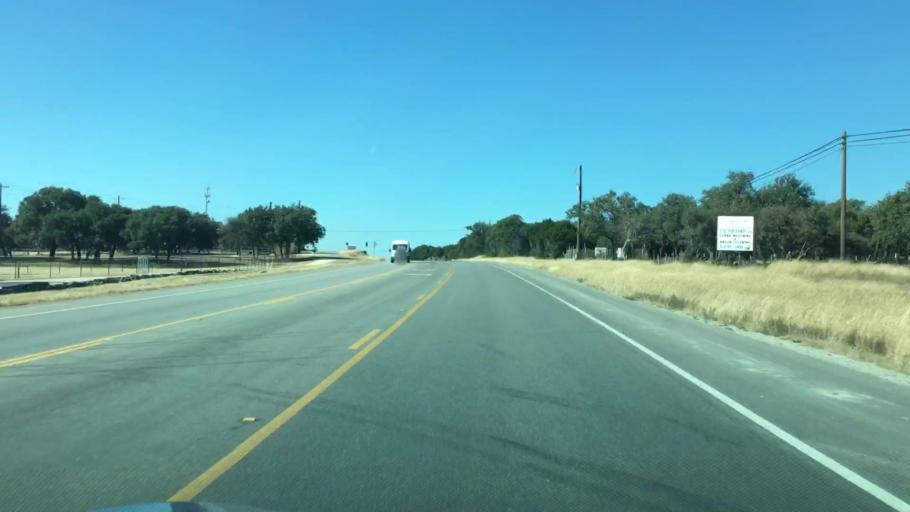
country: US
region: Texas
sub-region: Hays County
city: Dripping Springs
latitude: 30.2083
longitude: -98.1512
